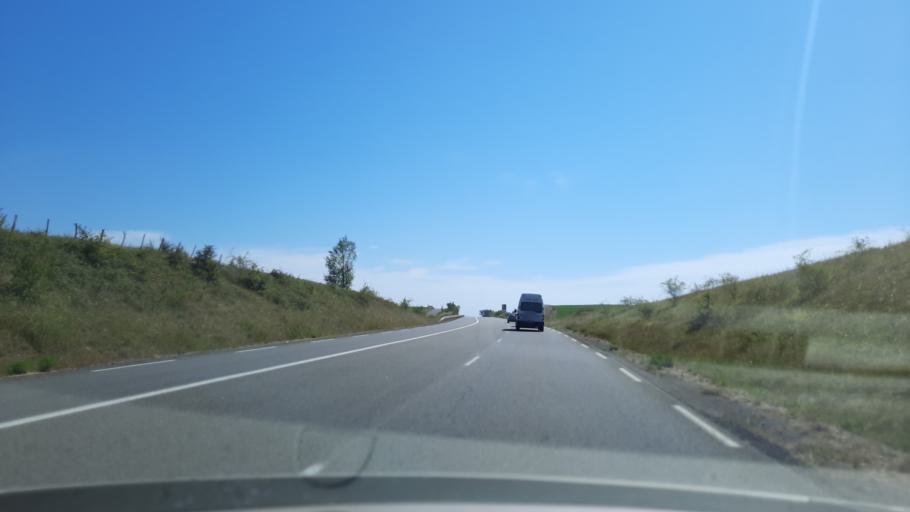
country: FR
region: Midi-Pyrenees
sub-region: Departement de l'Aveyron
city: Villefranche-de-Rouergue
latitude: 44.3425
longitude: 1.9454
